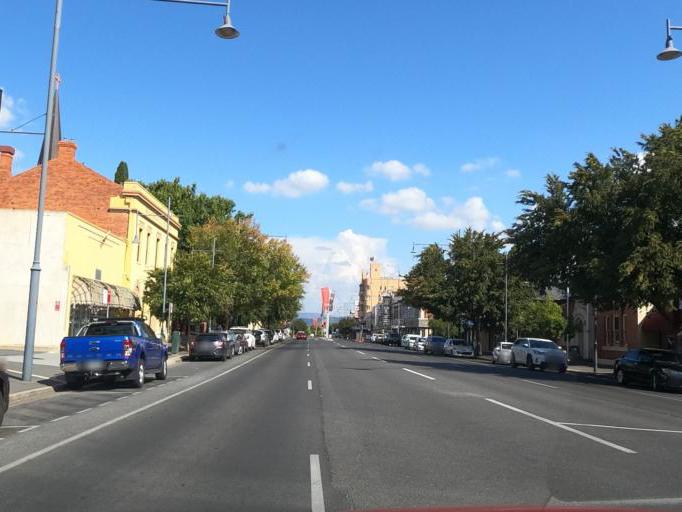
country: AU
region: New South Wales
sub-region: Albury Municipality
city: Albury
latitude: -36.0791
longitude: 146.9160
